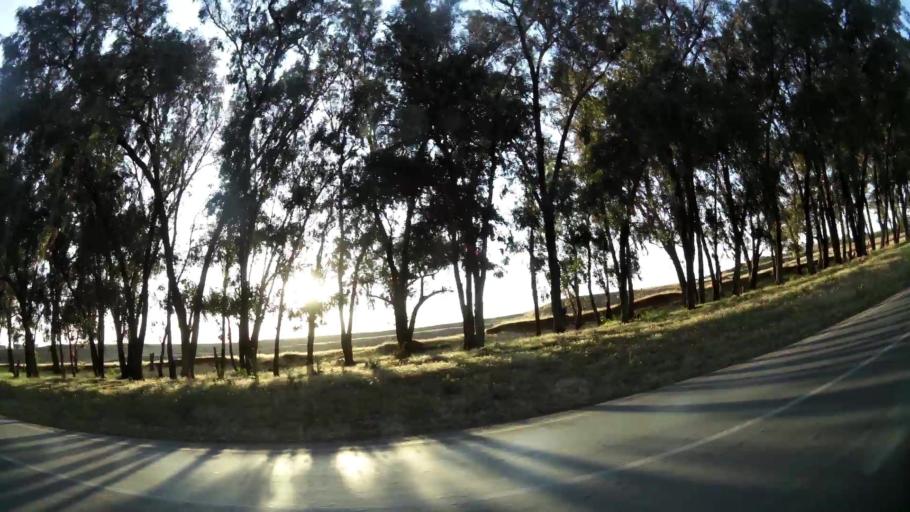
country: MA
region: Rabat-Sale-Zemmour-Zaer
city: Sale
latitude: 34.1323
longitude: -6.7316
